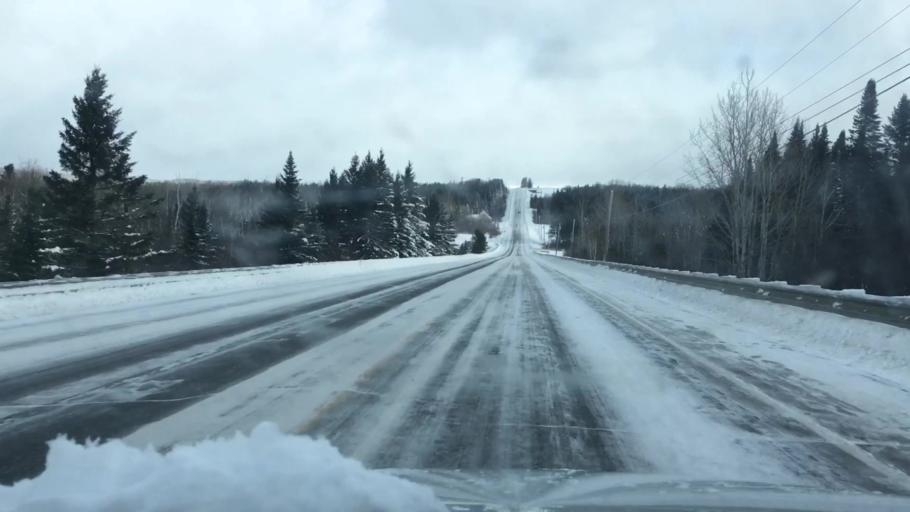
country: US
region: Maine
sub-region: Aroostook County
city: Van Buren
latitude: 47.0891
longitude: -67.9834
